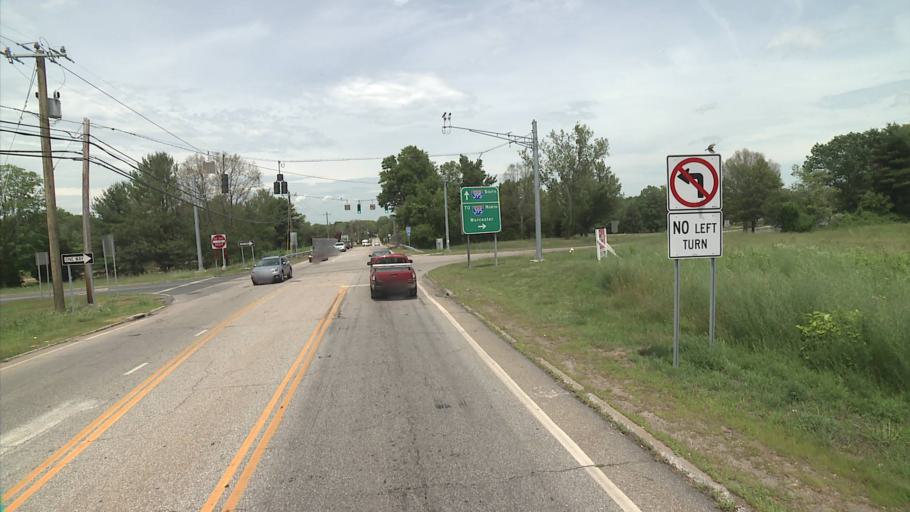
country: US
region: Connecticut
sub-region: New London County
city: Jewett City
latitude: 41.5899
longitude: -71.9759
